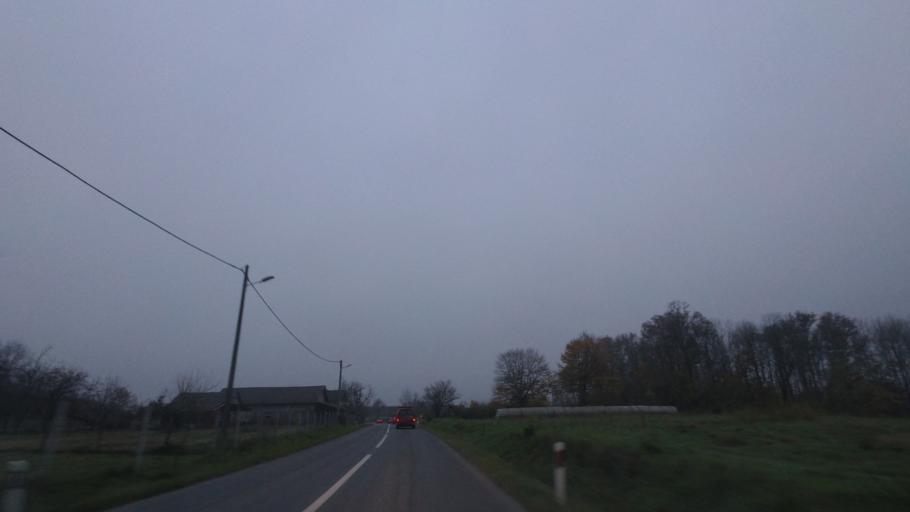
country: HR
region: Sisacko-Moslavacka
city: Petrinja
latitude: 45.4597
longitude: 16.2525
